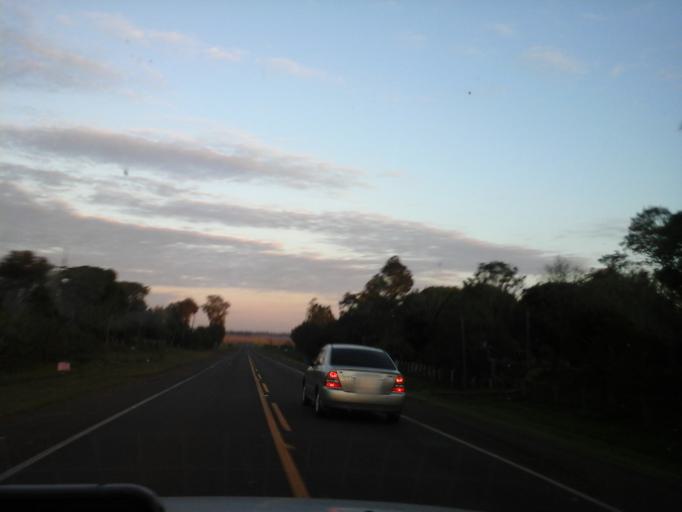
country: PY
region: Itapua
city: General Delgado
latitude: -27.0843
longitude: -56.5501
